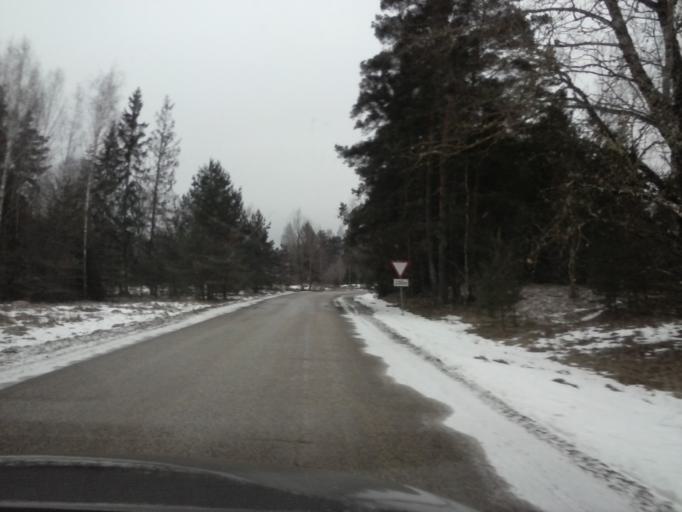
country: EE
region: Vorumaa
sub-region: Antsla vald
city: Vana-Antsla
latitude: 57.6159
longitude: 26.3996
